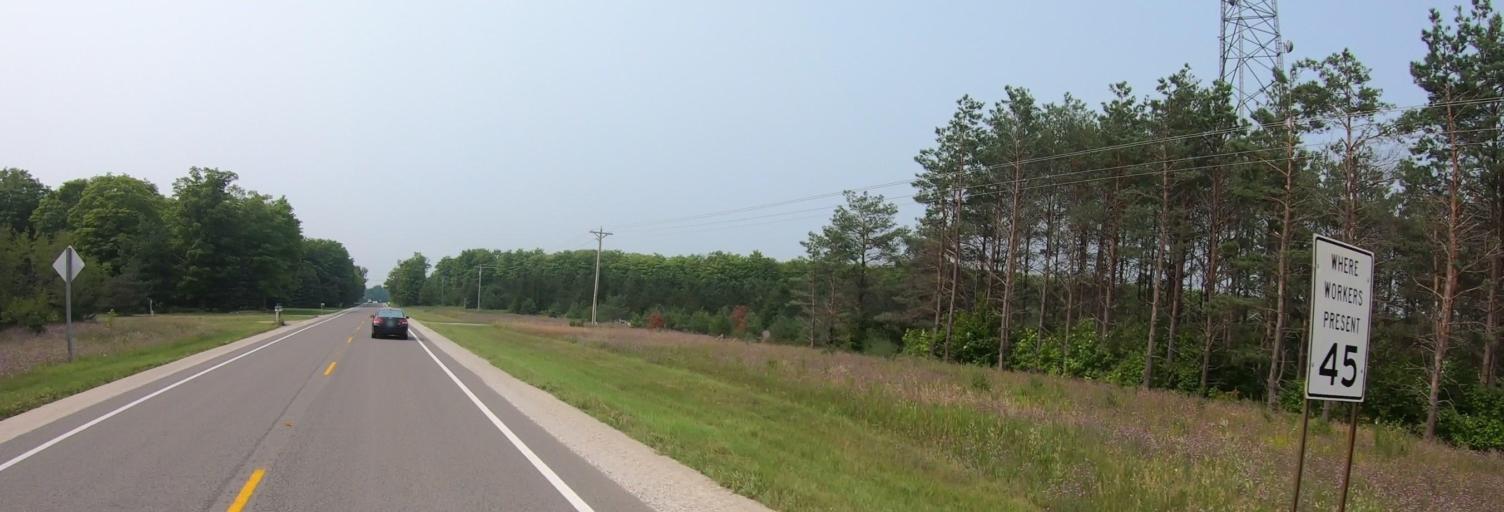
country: US
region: Michigan
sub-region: Chippewa County
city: Sault Ste. Marie
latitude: 46.0234
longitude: -84.0742
